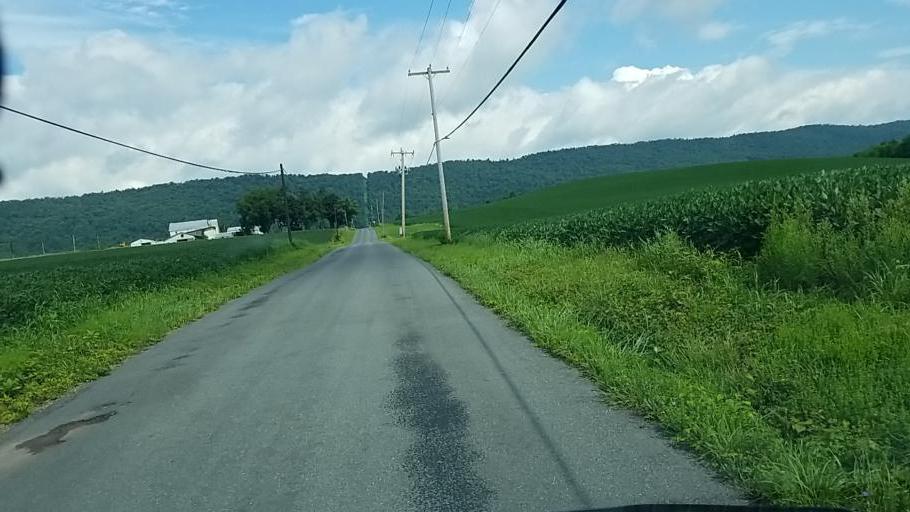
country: US
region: Pennsylvania
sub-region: Dauphin County
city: Millersburg
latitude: 40.5676
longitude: -76.9292
